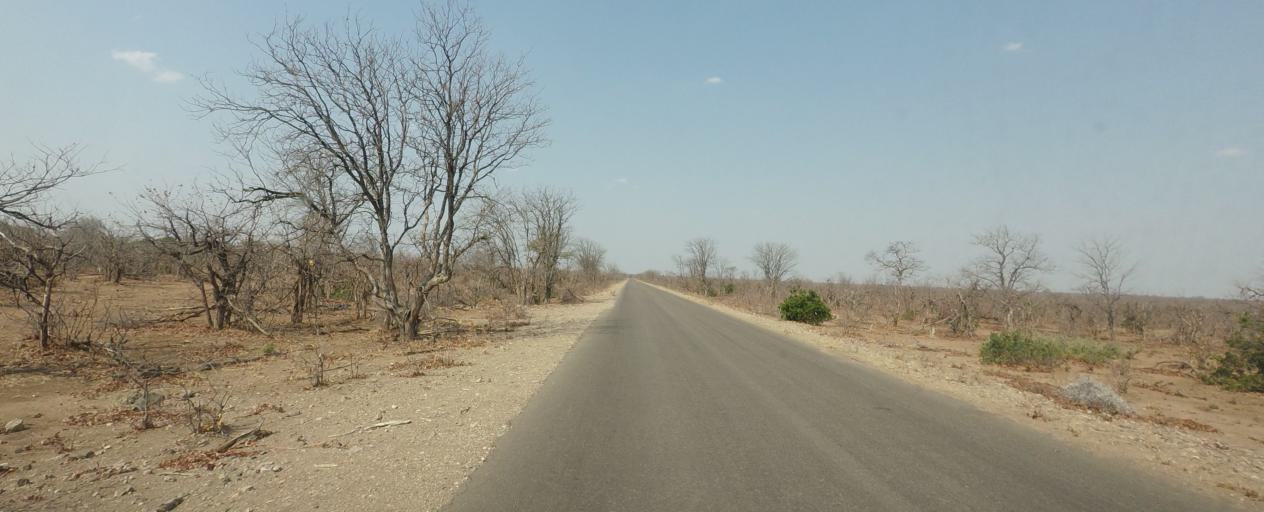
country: ZA
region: Limpopo
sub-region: Mopani District Municipality
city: Giyani
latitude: -23.1685
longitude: 31.3363
